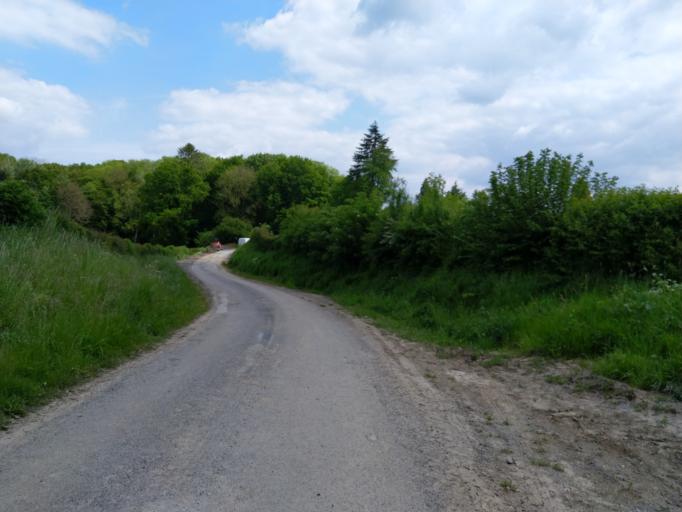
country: FR
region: Nord-Pas-de-Calais
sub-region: Departement du Nord
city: Le Quesnoy
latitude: 50.2453
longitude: 3.6743
